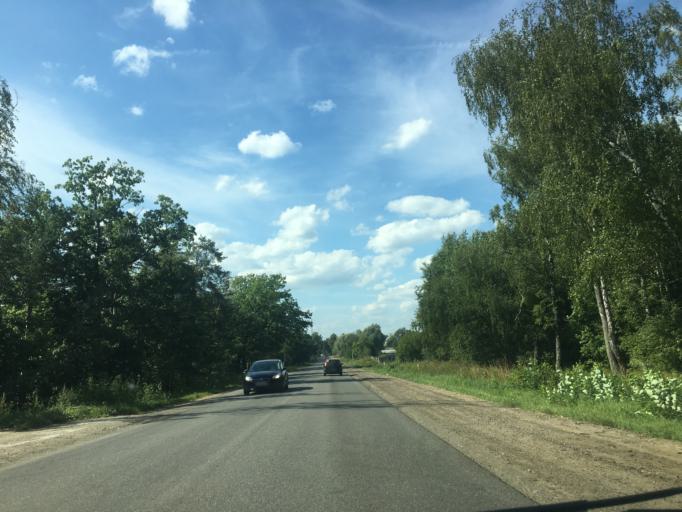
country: RU
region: Moskovskaya
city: Vidnoye
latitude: 55.5272
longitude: 37.6744
